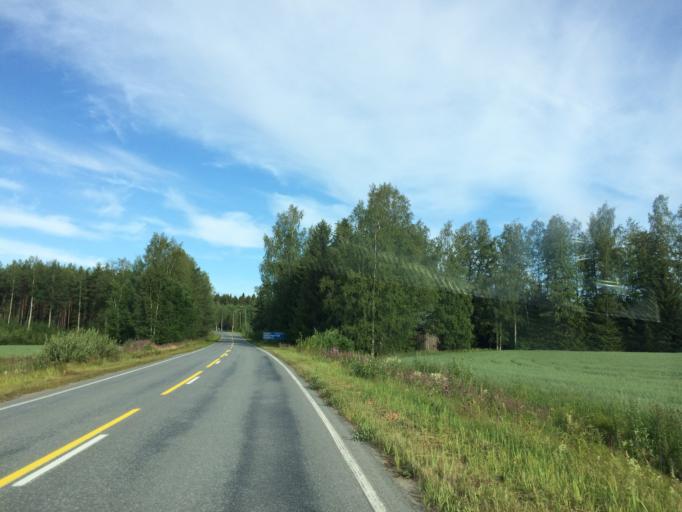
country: FI
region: Haeme
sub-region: Haemeenlinna
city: Haemeenlinna
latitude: 60.9403
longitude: 24.5257
